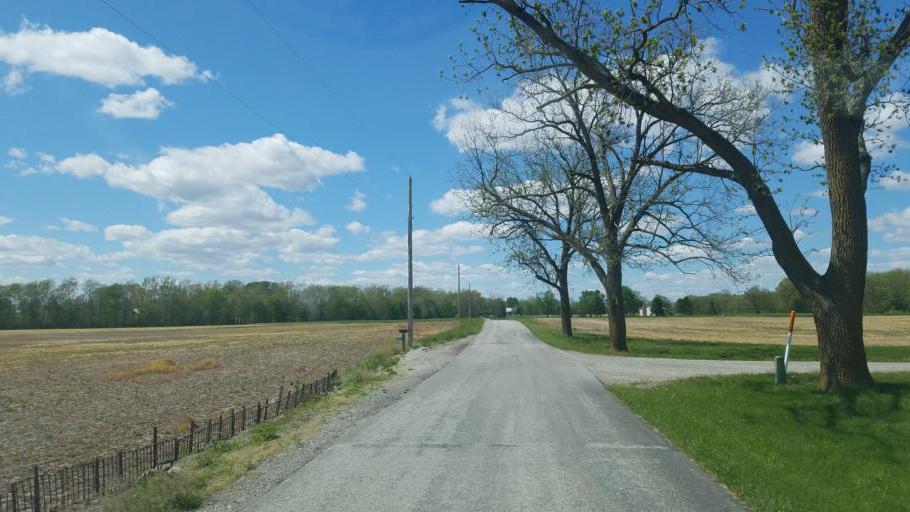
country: US
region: Ohio
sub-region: Marion County
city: Prospect
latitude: 40.4082
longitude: -83.1912
